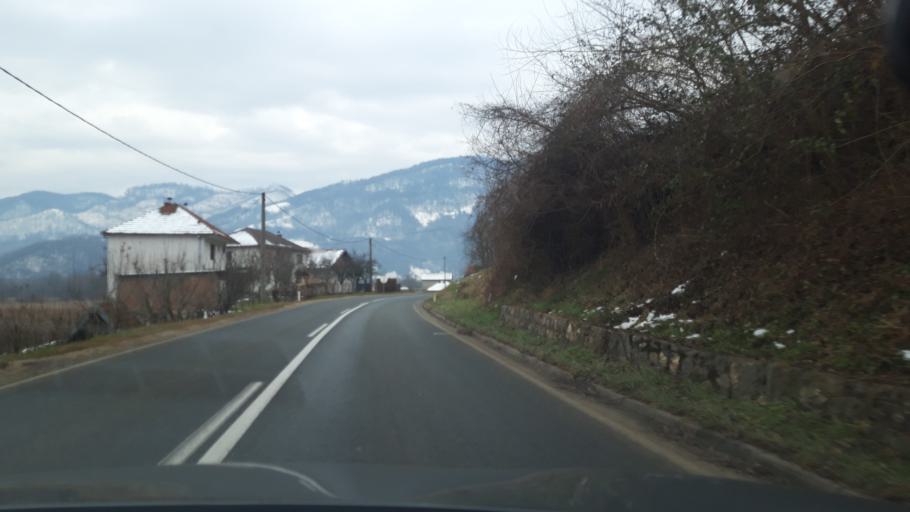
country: RS
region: Central Serbia
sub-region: Macvanski Okrug
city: Mali Zvornik
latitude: 44.2938
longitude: 19.1495
